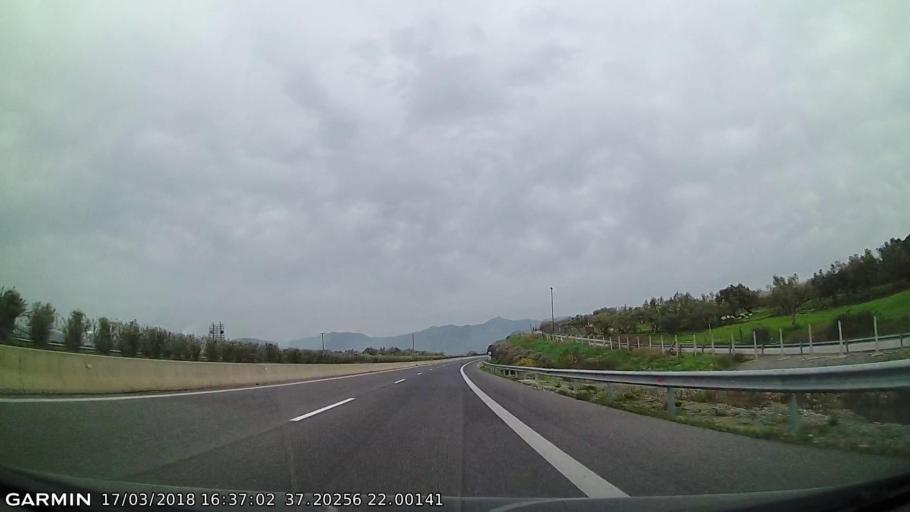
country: GR
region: Peloponnese
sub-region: Nomos Messinias
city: Meligalas
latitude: 37.2035
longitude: 22.0011
